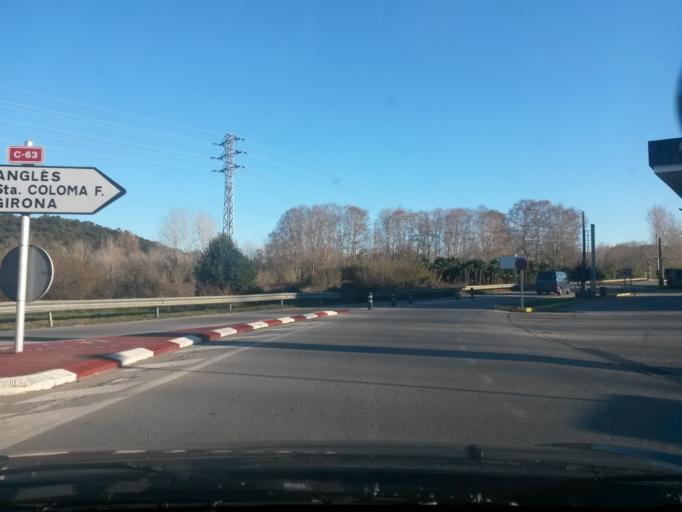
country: ES
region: Catalonia
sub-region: Provincia de Girona
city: la Cellera de Ter
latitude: 41.9671
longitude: 2.6249
